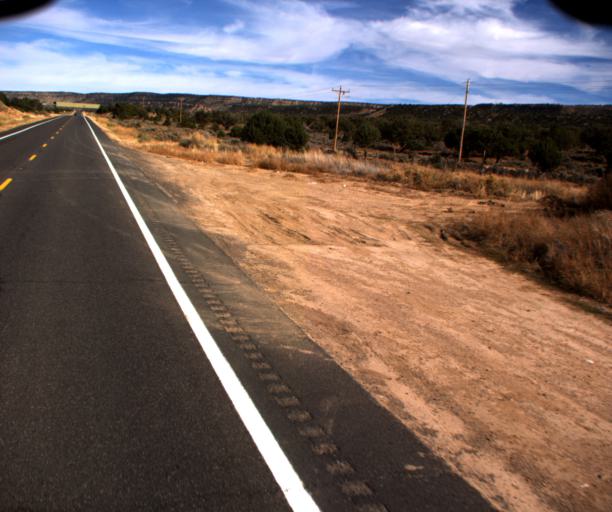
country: US
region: Arizona
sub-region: Navajo County
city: Kayenta
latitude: 36.5536
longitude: -110.5198
